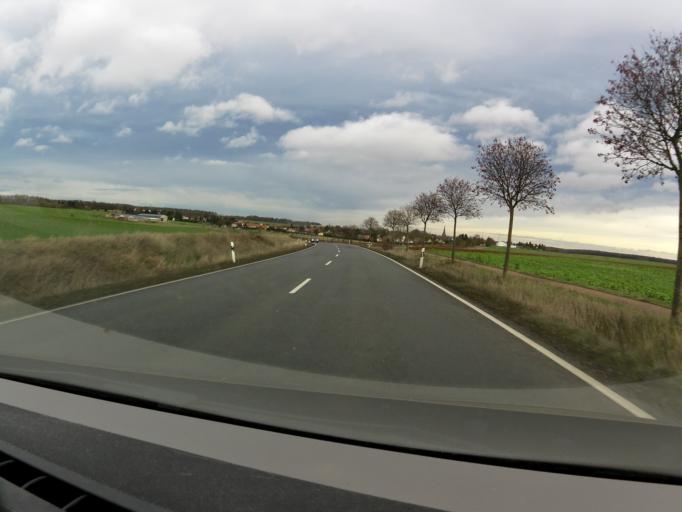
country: DE
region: Saxony-Anhalt
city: Blankenheim
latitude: 51.5437
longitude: 11.3953
